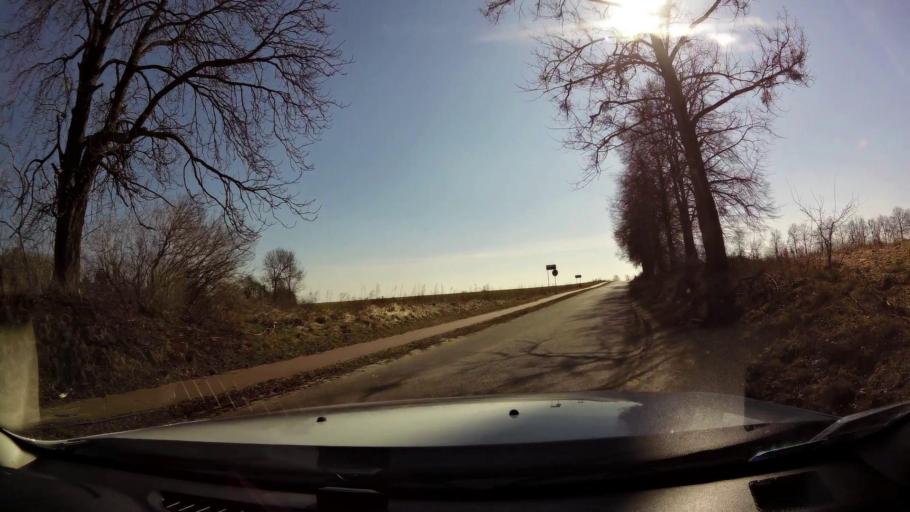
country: PL
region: West Pomeranian Voivodeship
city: Trzcinsko Zdroj
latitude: 52.9838
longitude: 14.6070
